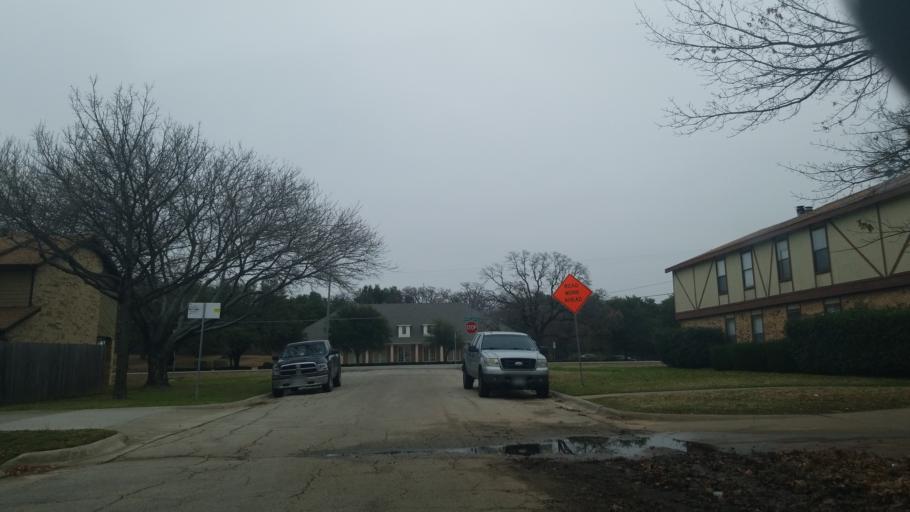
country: US
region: Texas
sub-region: Denton County
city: Denton
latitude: 33.1754
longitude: -97.1426
